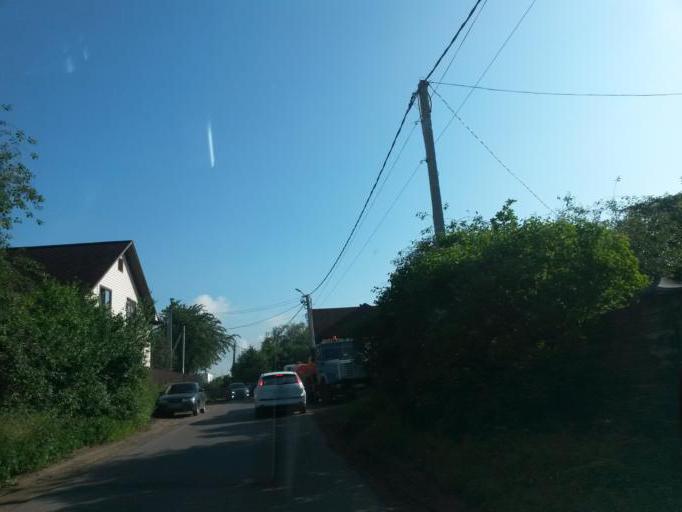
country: RU
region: Moscow
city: Zyablikovo
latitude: 55.5882
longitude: 37.7837
